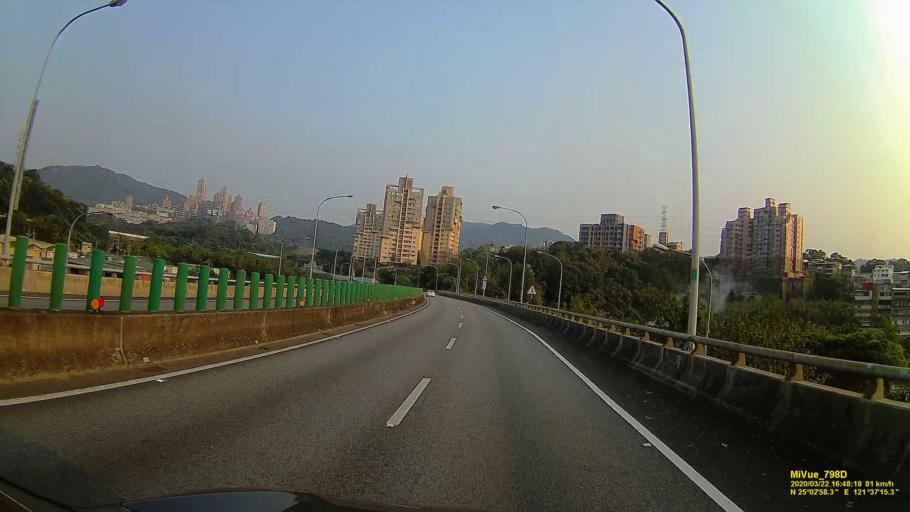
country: TW
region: Taipei
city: Taipei
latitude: 25.0488
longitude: 121.6210
